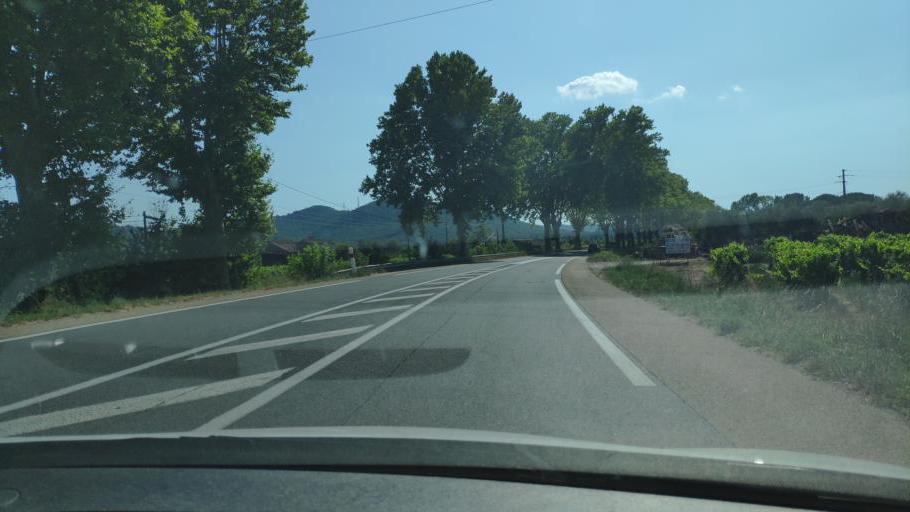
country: FR
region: Provence-Alpes-Cote d'Azur
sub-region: Departement du Var
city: Les Arcs
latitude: 43.4443
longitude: 6.4676
